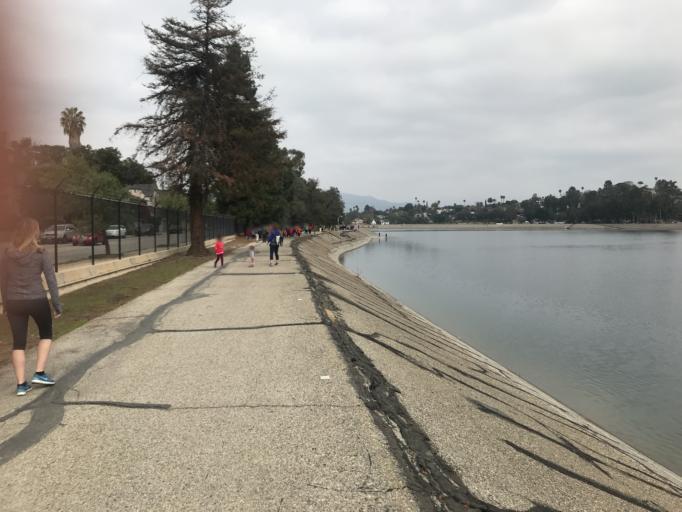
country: US
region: California
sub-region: Los Angeles County
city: Silver Lake
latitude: 34.0972
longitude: -118.2664
